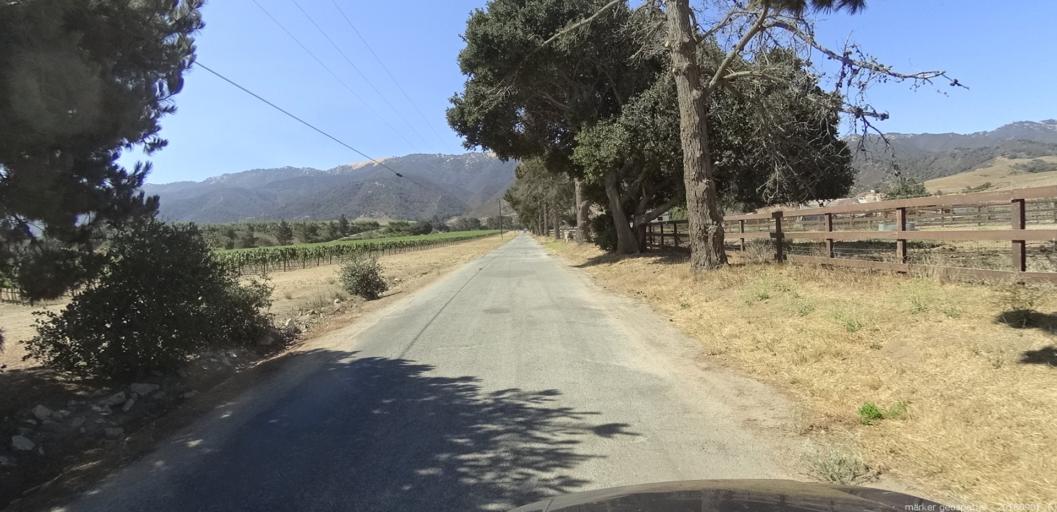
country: US
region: California
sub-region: Monterey County
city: Chualar
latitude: 36.5213
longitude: -121.5217
